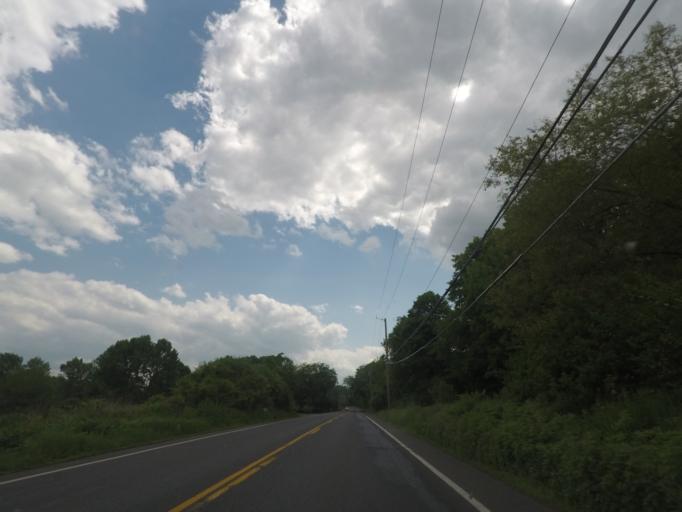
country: US
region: New York
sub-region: Dutchess County
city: Dover Plains
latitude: 41.8734
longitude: -73.5381
